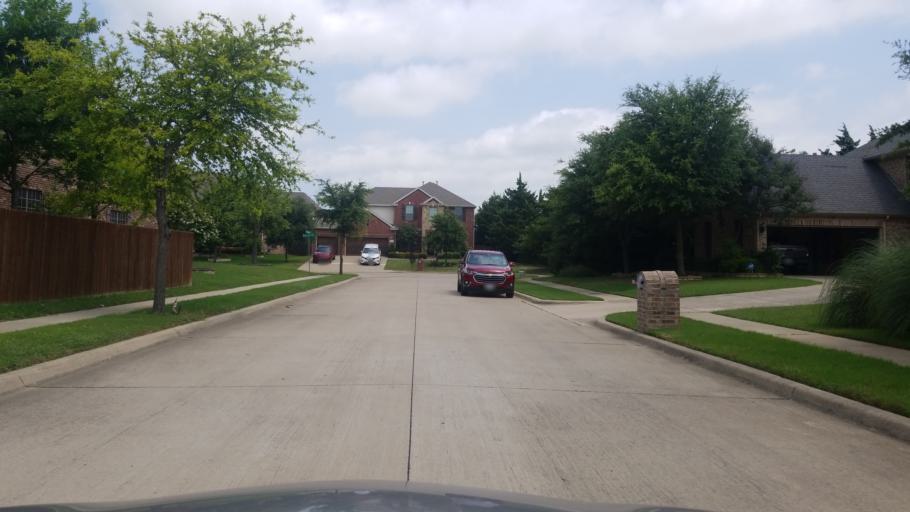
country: US
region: Texas
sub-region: Dallas County
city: Duncanville
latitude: 32.6848
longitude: -96.9355
